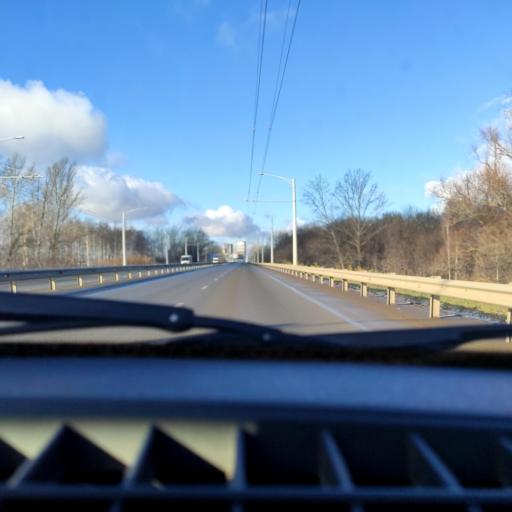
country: RU
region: Bashkortostan
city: Ufa
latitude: 54.7672
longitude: 55.9324
